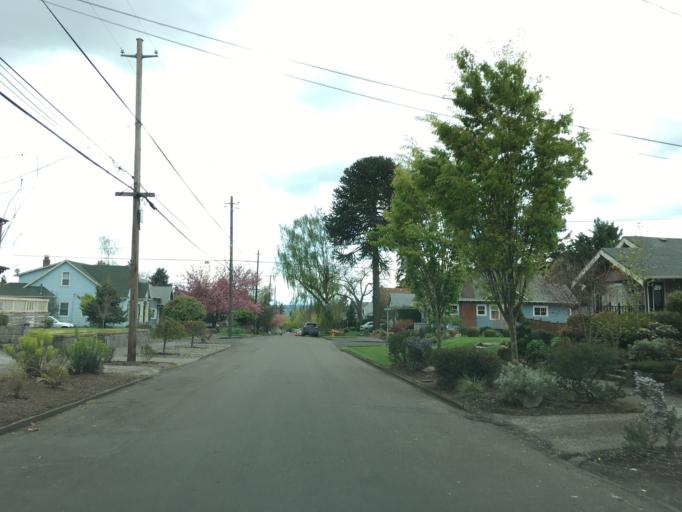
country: US
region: Oregon
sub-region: Multnomah County
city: Lents
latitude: 45.5505
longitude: -122.5878
